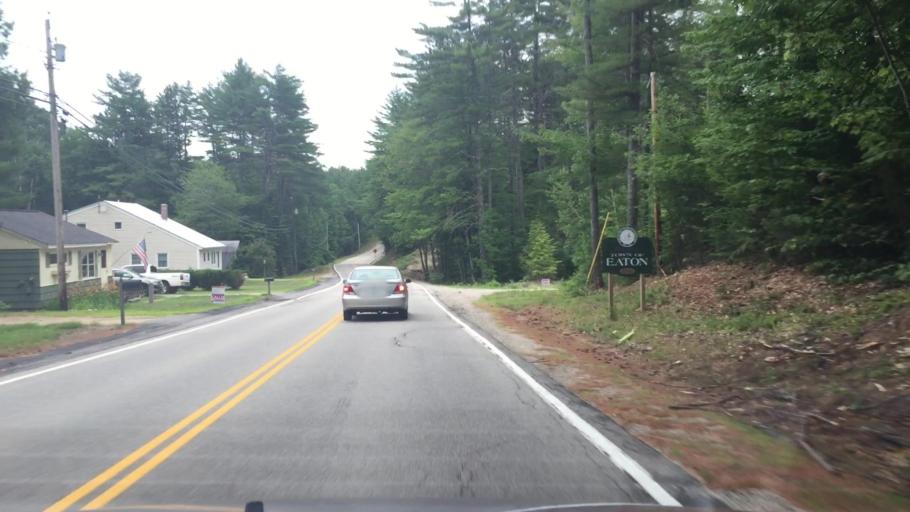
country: US
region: New Hampshire
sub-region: Carroll County
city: Conway
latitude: 43.9272
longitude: -71.0819
